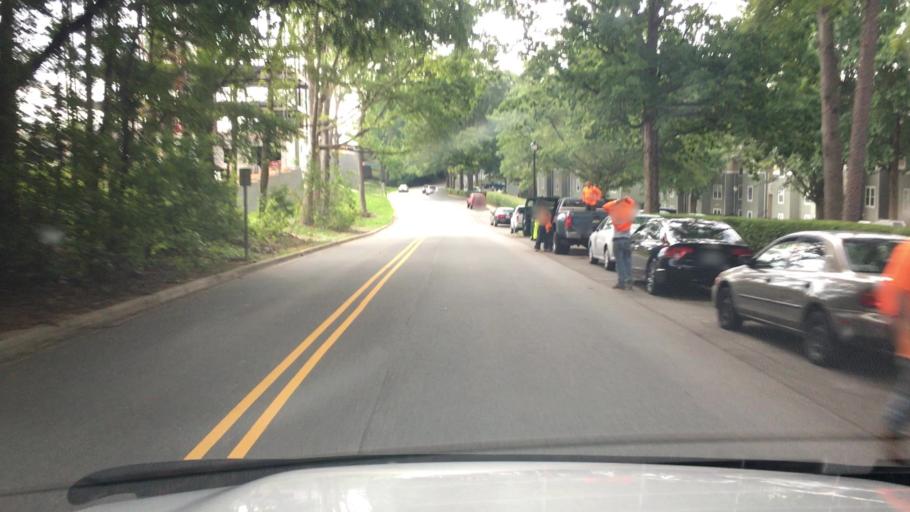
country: US
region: North Carolina
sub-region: Mecklenburg County
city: Cornelius
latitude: 35.4850
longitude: -80.8876
